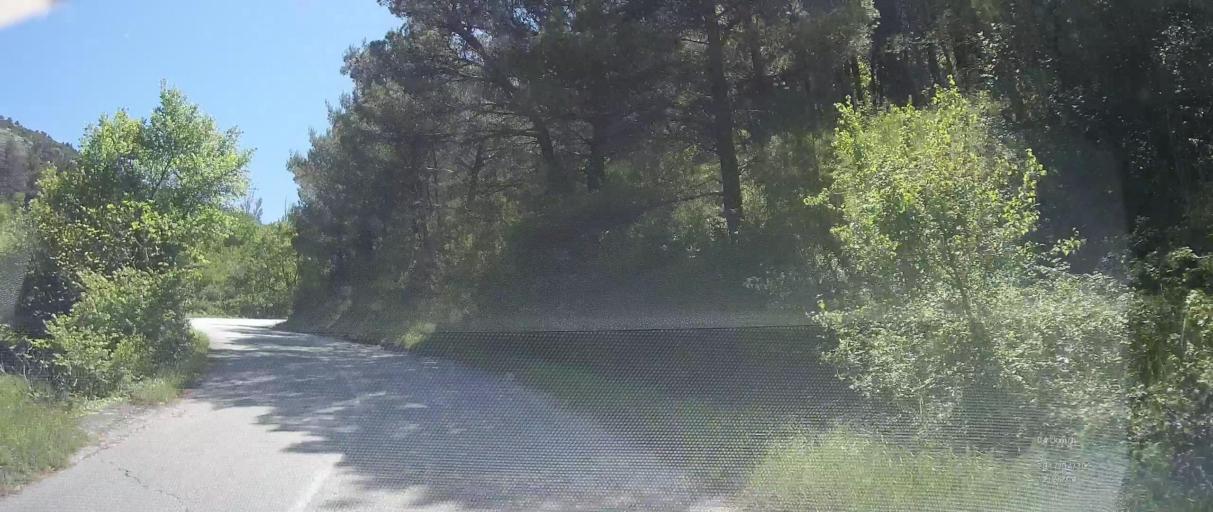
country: HR
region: Splitsko-Dalmatinska
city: Srinjine
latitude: 43.5040
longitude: 16.5991
